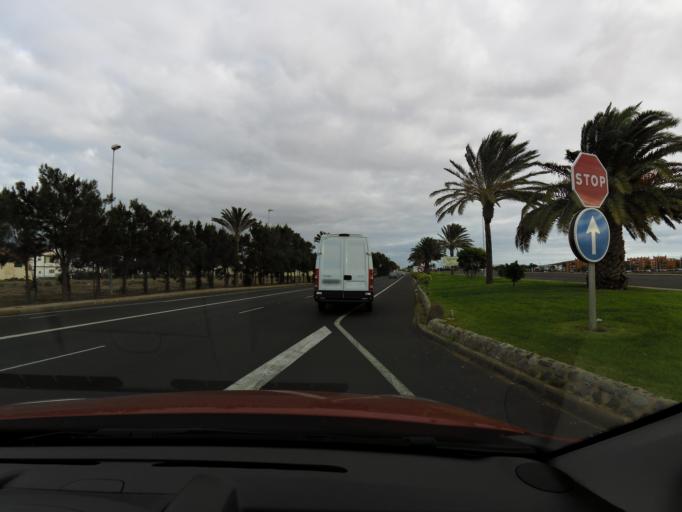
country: ES
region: Canary Islands
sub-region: Provincia de Las Palmas
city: Cruce de Arinaga
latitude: 27.8723
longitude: -15.4276
